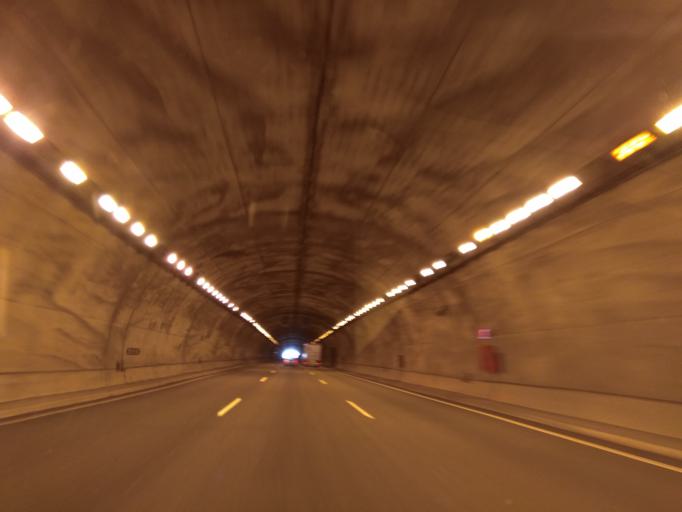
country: ES
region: Cantabria
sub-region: Provincia de Cantabria
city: Cartes
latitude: 43.3055
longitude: -4.0788
